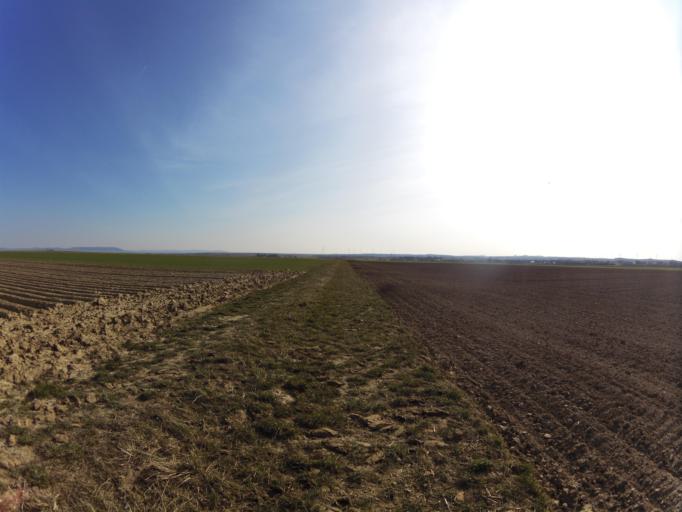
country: DE
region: Bavaria
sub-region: Regierungsbezirk Unterfranken
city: Prosselsheim
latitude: 49.8357
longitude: 10.1164
